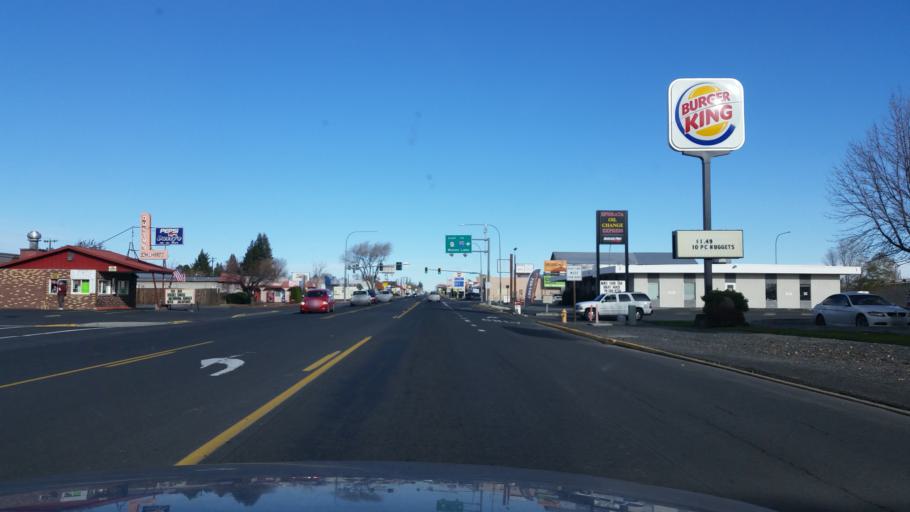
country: US
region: Washington
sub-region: Grant County
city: Ephrata
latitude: 47.3072
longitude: -119.5612
